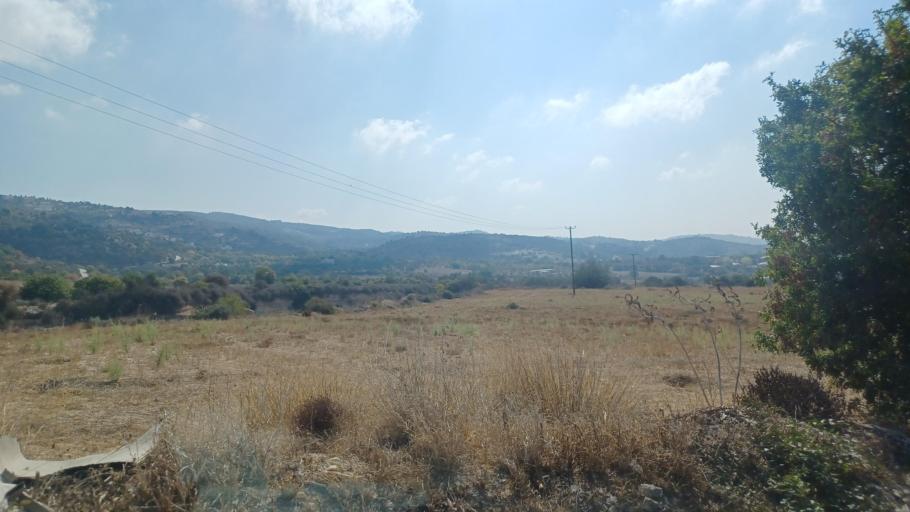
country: CY
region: Pafos
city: Mesogi
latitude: 34.8322
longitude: 32.4549
